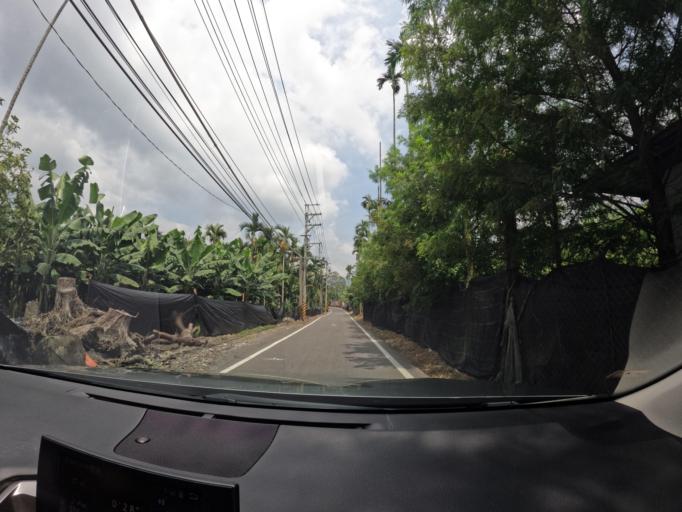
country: TW
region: Taiwan
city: Lugu
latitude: 23.8095
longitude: 120.8246
